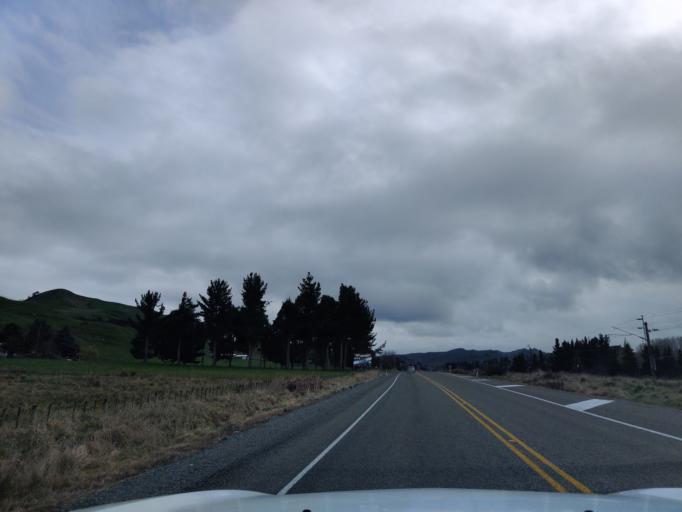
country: NZ
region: Manawatu-Wanganui
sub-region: Ruapehu District
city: Waiouru
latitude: -39.7281
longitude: 175.8429
